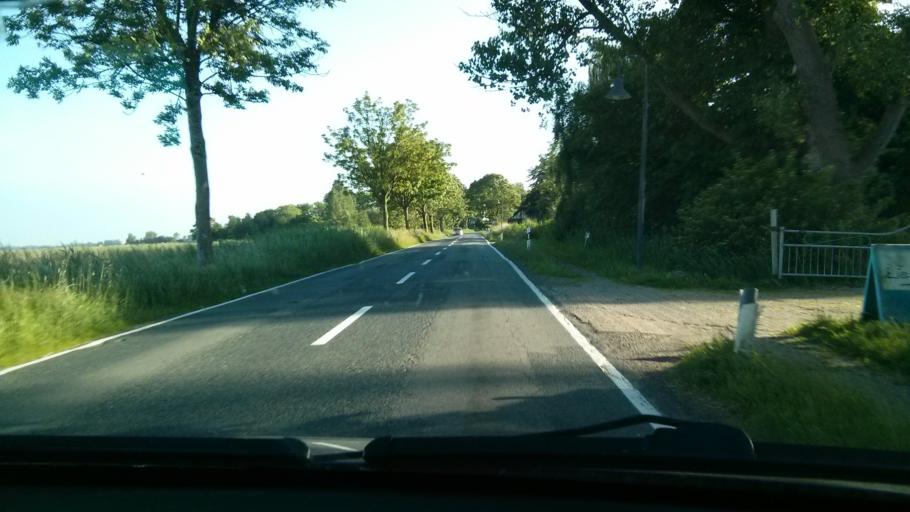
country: DE
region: Lower Saxony
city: Nordenham
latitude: 53.4713
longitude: 8.5437
